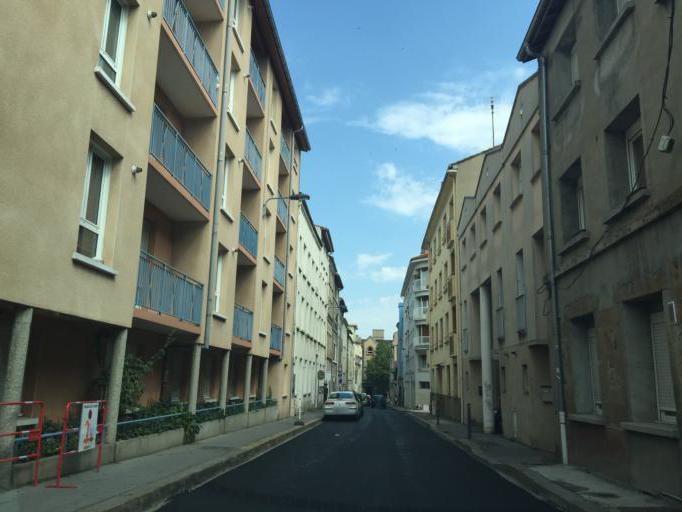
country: FR
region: Rhone-Alpes
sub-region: Departement de la Loire
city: Saint-Etienne
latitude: 45.4307
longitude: 4.3926
